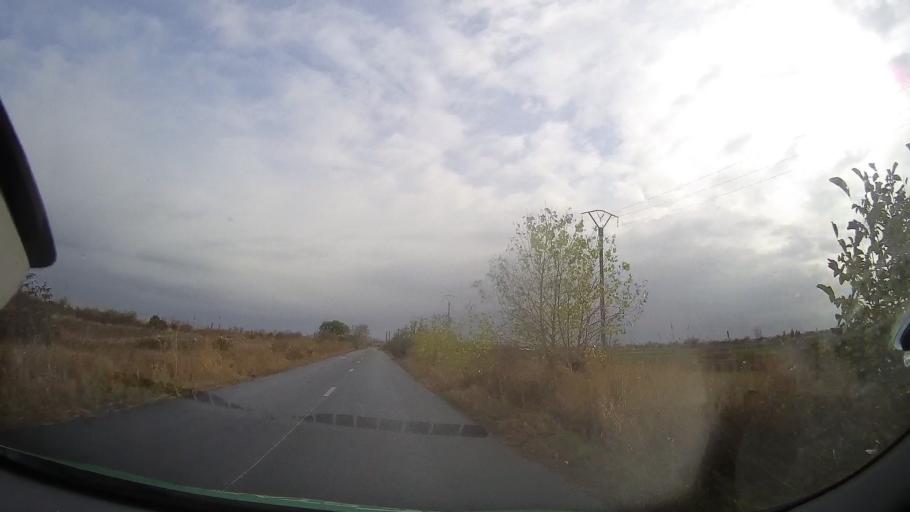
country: RO
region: Ialomita
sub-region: Comuna Maia
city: Maia
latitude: 44.7467
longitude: 26.3968
